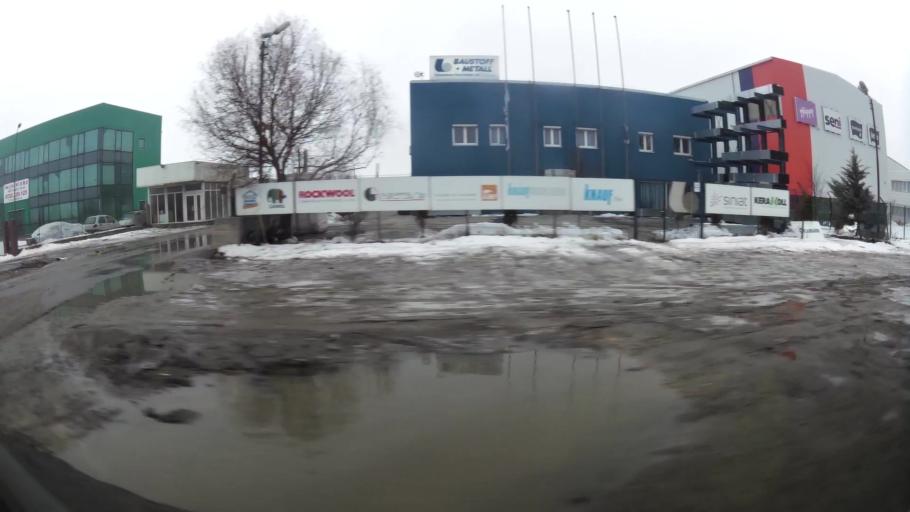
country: RO
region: Ilfov
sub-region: Comuna Bragadiru
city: Bragadiru
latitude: 44.3962
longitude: 25.9818
